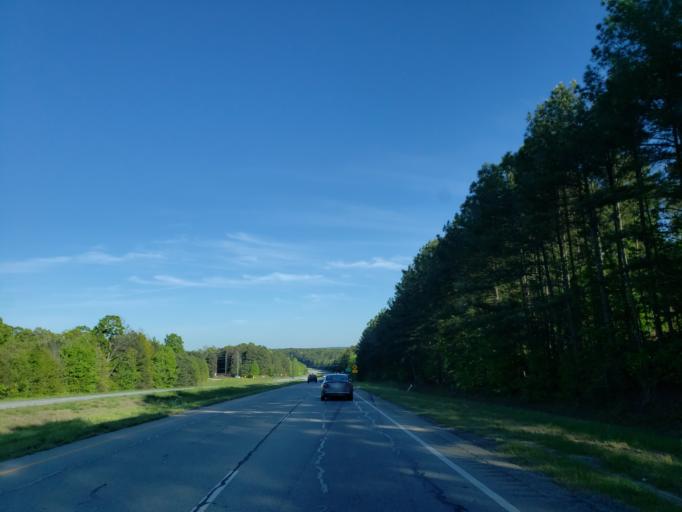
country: US
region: Georgia
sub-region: Paulding County
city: Dallas
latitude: 33.9210
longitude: -84.9323
